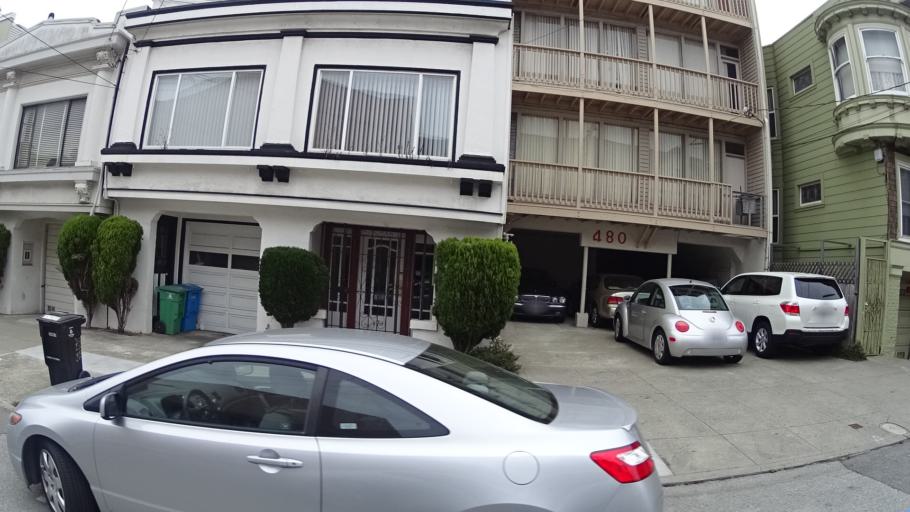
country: US
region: California
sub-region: San Francisco County
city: San Francisco
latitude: 37.7794
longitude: -122.4673
